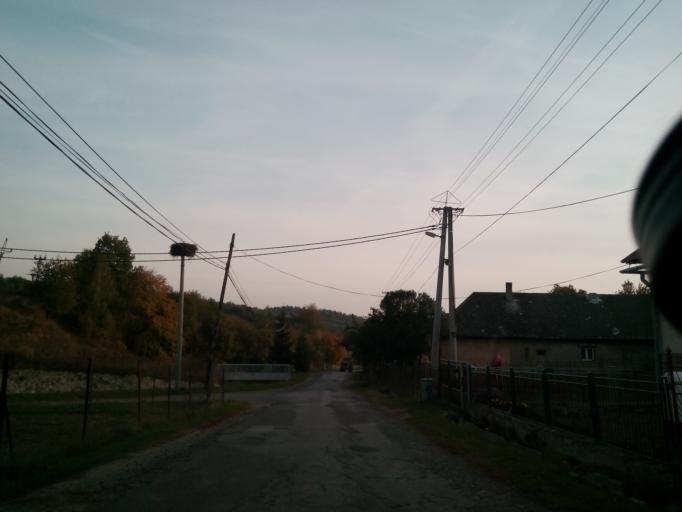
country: SK
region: Presovsky
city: Svidnik
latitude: 49.3904
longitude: 21.4938
